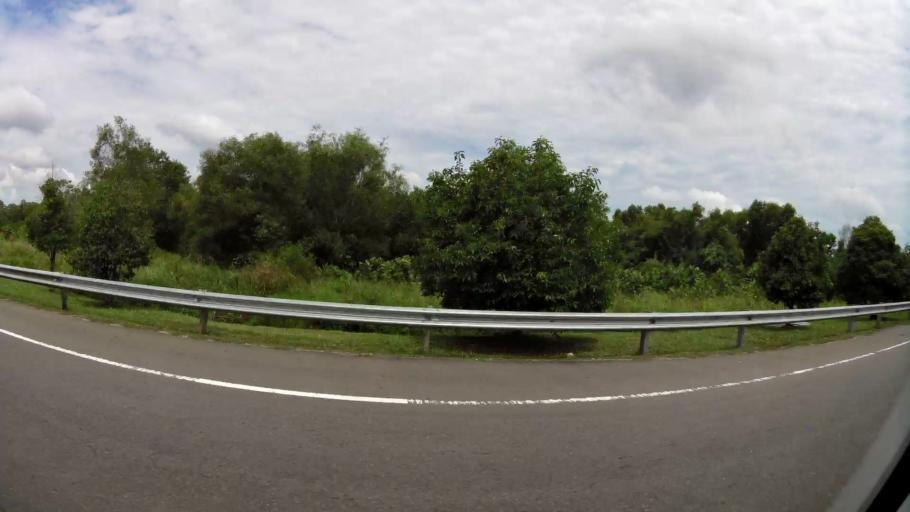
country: BN
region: Brunei and Muara
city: Bandar Seri Begawan
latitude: 4.9254
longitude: 114.9225
